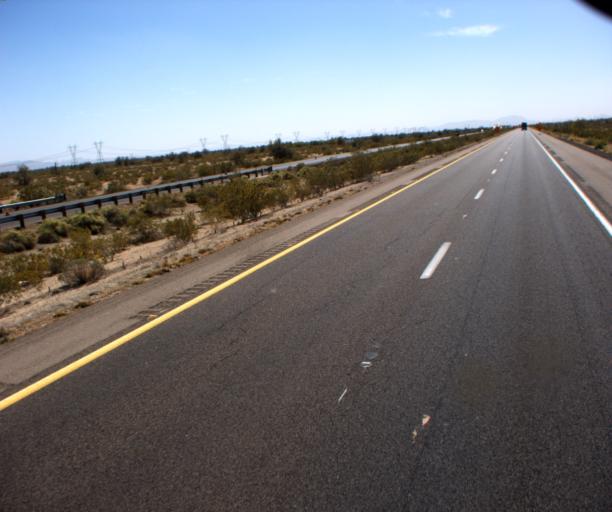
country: US
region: Arizona
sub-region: Maricopa County
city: Gila Bend
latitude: 33.0060
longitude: -112.6567
